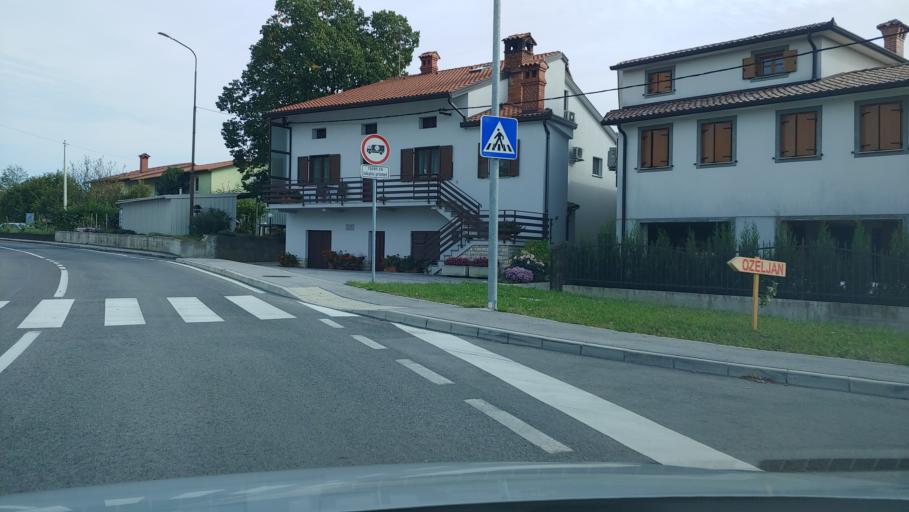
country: SI
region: Nova Gorica
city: Sempas
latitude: 45.8936
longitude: 13.7906
